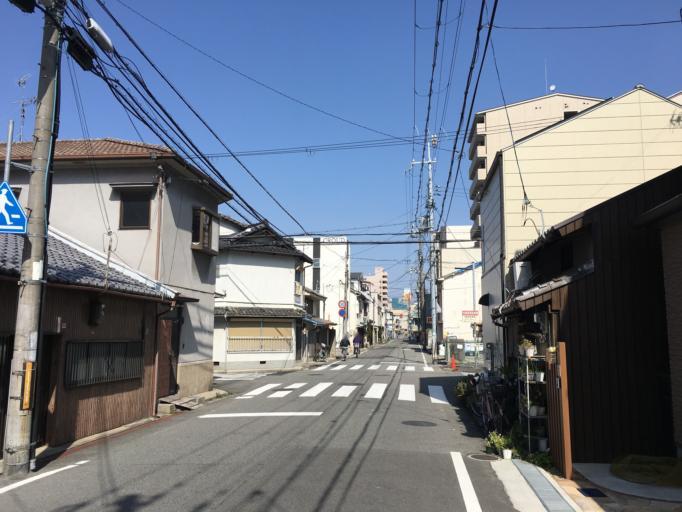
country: JP
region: Hyogo
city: Amagasaki
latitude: 34.7193
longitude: 135.4077
